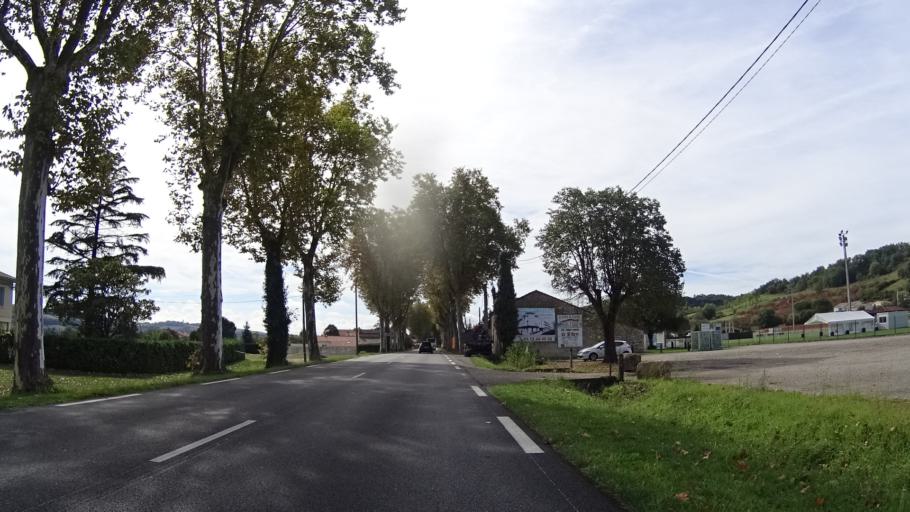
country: FR
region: Aquitaine
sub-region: Departement du Lot-et-Garonne
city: Layrac
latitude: 44.1265
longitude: 0.6591
